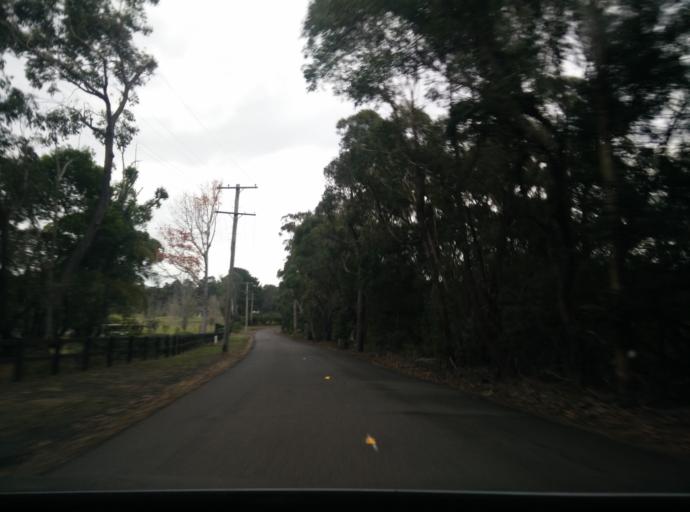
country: AU
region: New South Wales
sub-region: Gosford Shire
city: Narara
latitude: -33.3643
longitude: 151.3140
